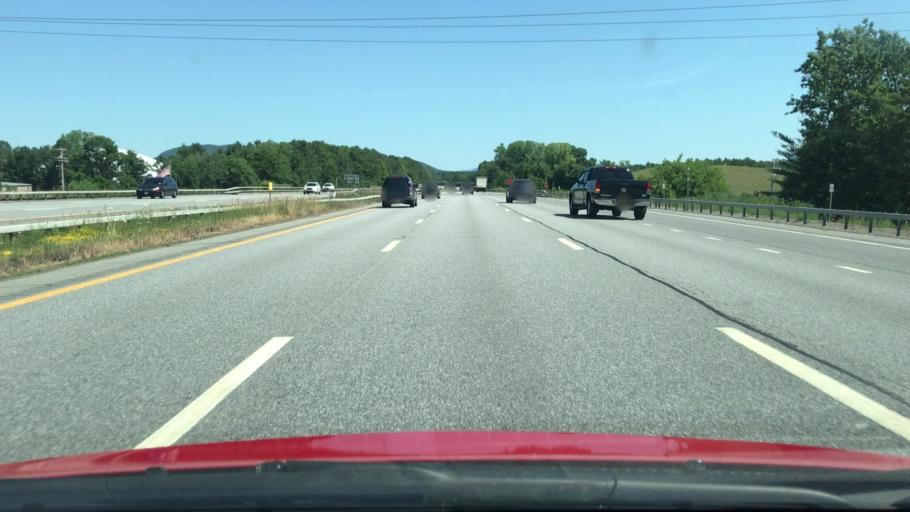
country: US
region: New York
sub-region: Warren County
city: West Glens Falls
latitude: 43.3014
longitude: -73.6779
